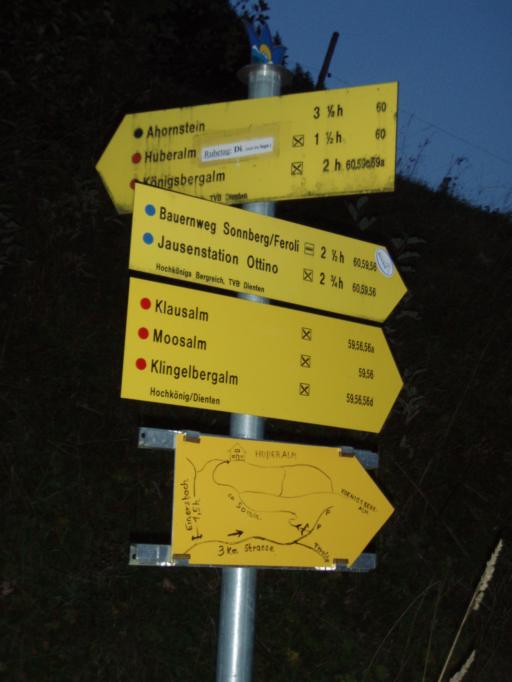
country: AT
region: Salzburg
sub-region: Politischer Bezirk Zell am See
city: Dienten am Hochkonig
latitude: 47.3561
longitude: 13.0010
